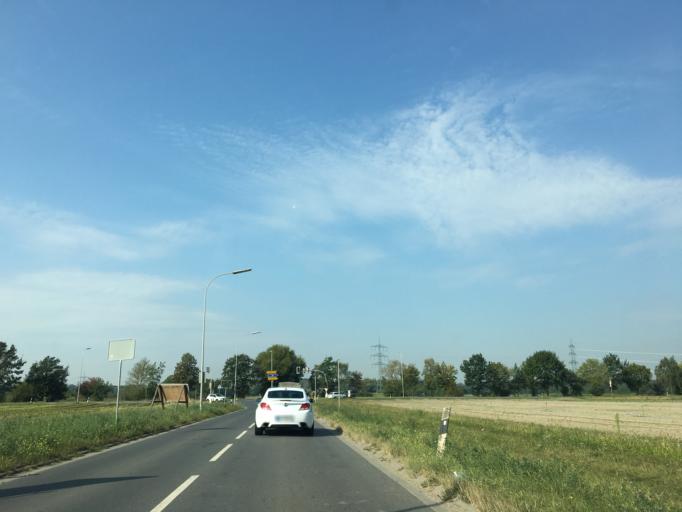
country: DE
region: Hesse
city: Griesheim
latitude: 49.8681
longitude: 8.5436
